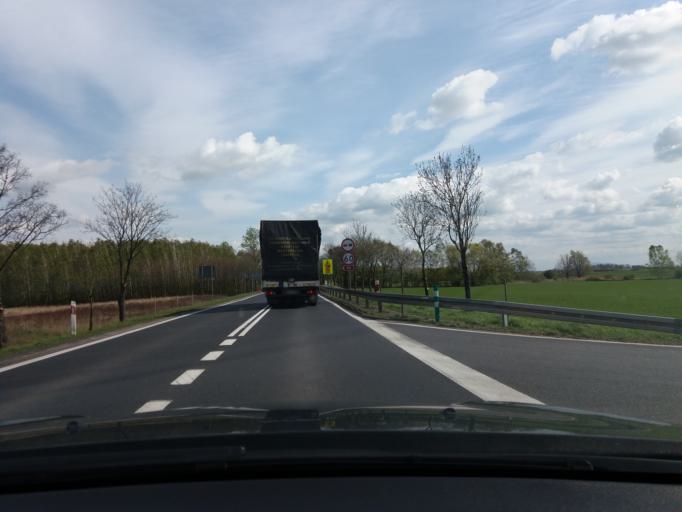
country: PL
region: Lower Silesian Voivodeship
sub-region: Powiat sredzki
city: Ciechow
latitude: 51.1717
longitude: 16.5421
